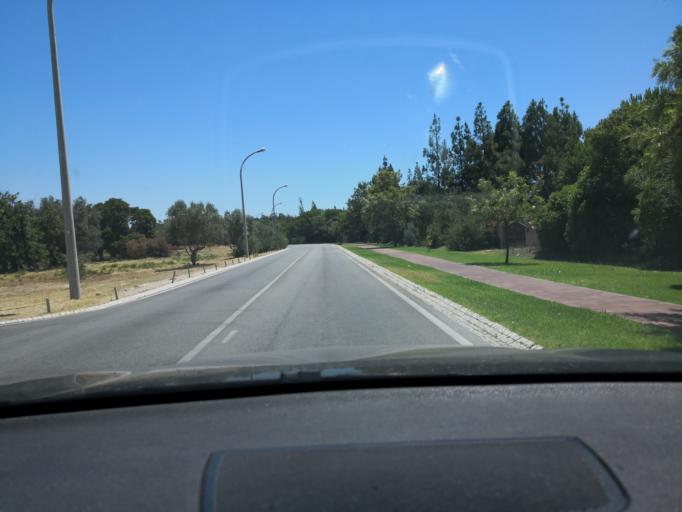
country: PT
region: Faro
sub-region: Loule
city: Vilamoura
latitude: 37.1046
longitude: -8.1288
